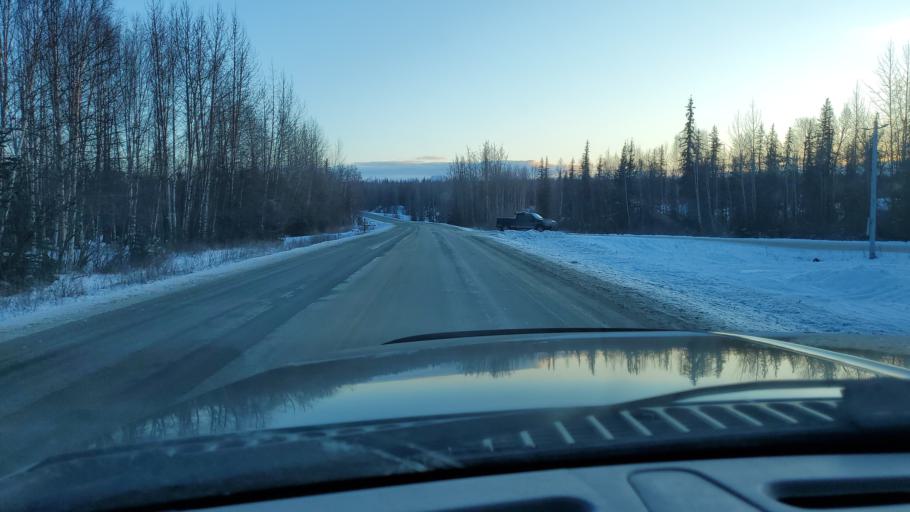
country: US
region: Alaska
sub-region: Matanuska-Susitna Borough
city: Fishhook
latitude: 61.6854
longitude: -149.2401
